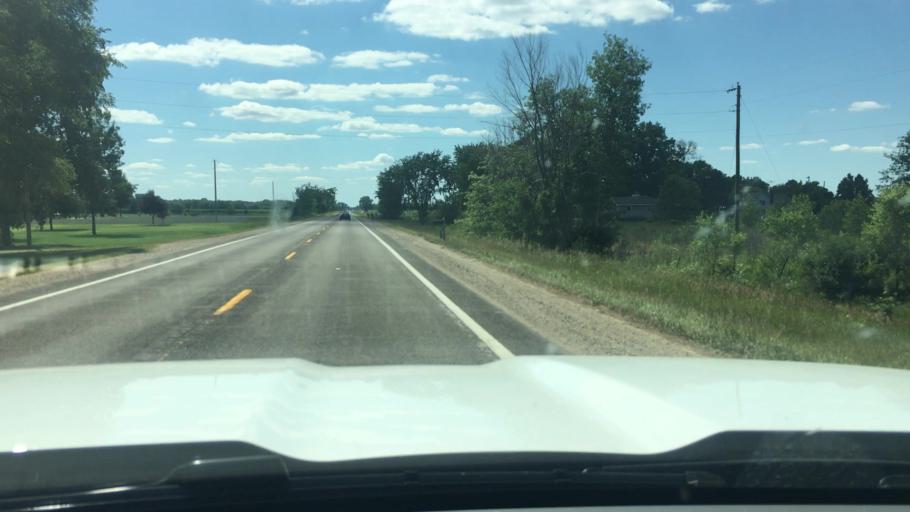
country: US
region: Michigan
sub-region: Clinton County
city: Ovid
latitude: 43.1760
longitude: -84.4114
